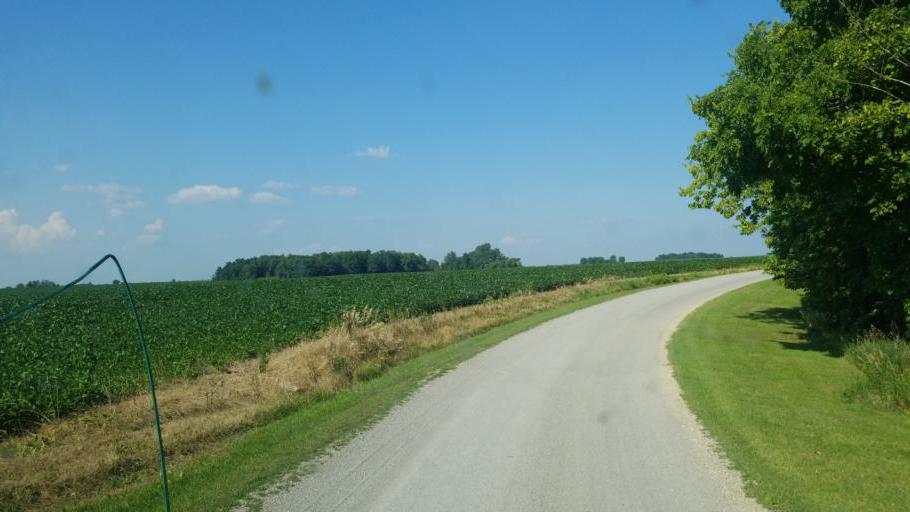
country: US
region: Ohio
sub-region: Wyandot County
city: Upper Sandusky
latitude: 40.7890
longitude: -83.3355
